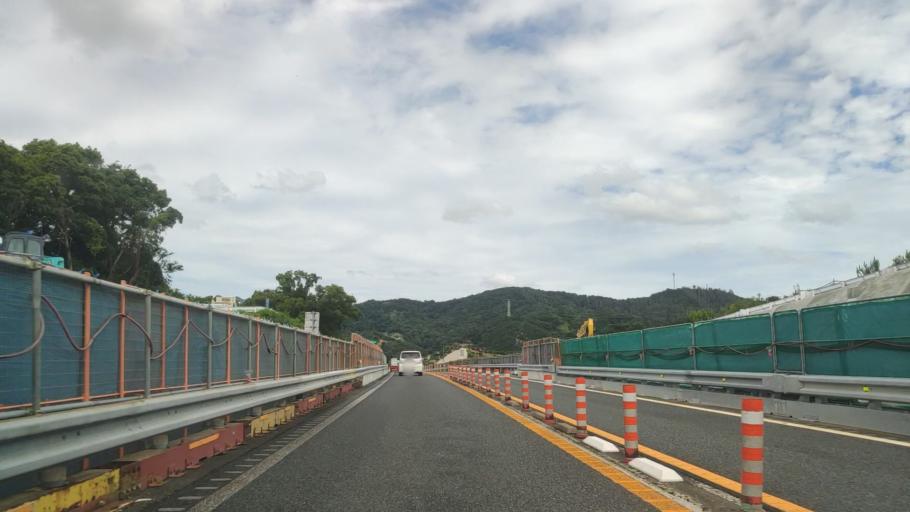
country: JP
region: Wakayama
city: Gobo
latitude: 33.9092
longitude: 135.1941
